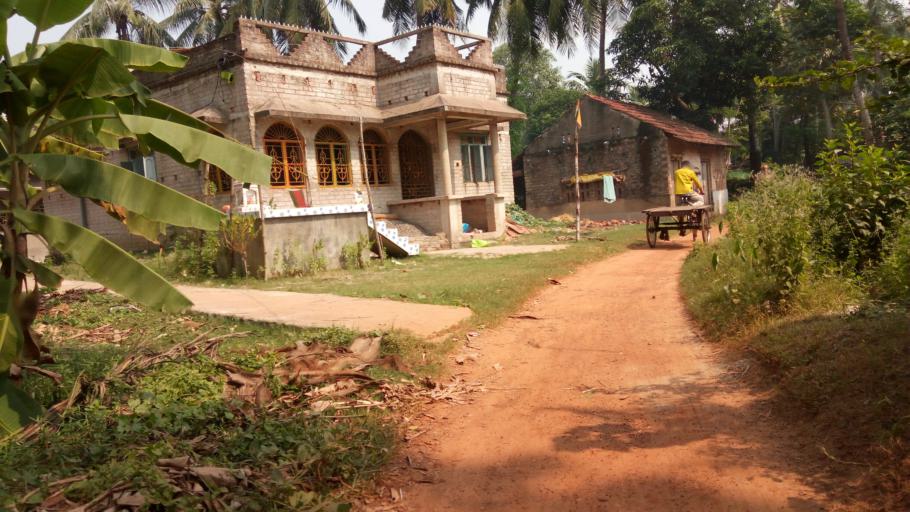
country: IN
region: West Bengal
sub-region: Purba Medinipur
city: Mahishadal
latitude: 22.1704
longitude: 87.9133
